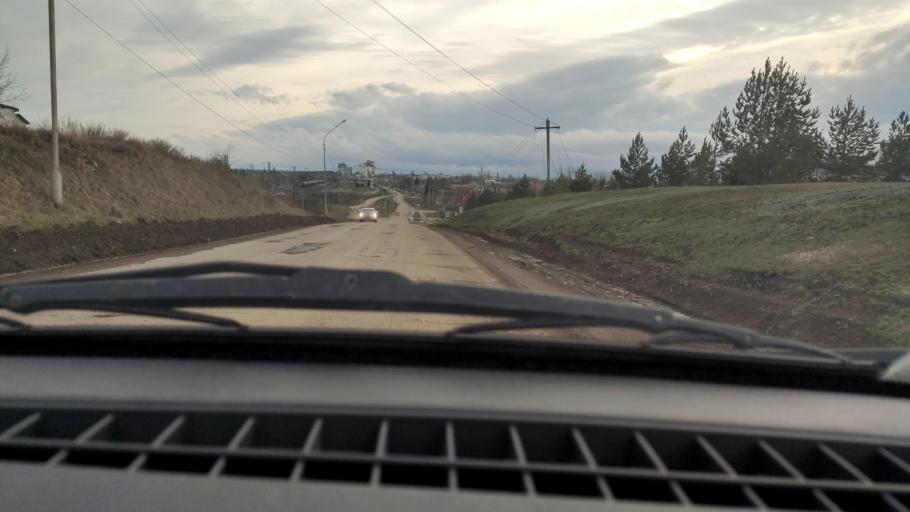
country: RU
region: Bashkortostan
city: Davlekanovo
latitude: 54.2215
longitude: 55.0368
